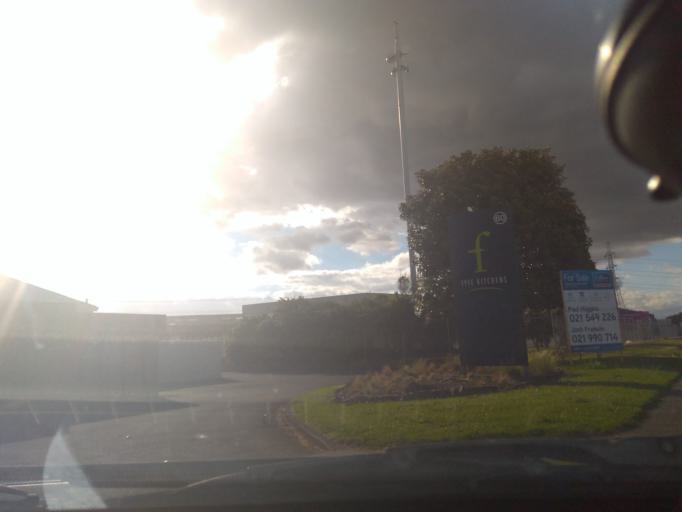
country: NZ
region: Auckland
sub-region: Auckland
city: Manukau City
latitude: -36.9402
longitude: 174.8866
